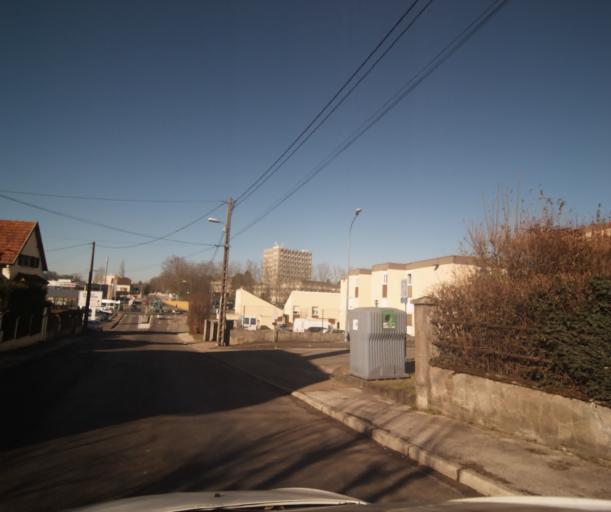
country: FR
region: Franche-Comte
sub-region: Departement du Doubs
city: Besancon
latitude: 47.2429
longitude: 5.9966
